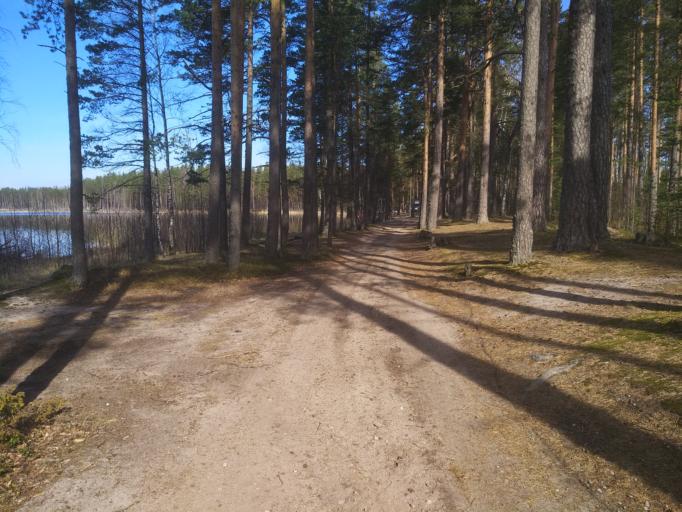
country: RU
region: Leningrad
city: Priozersk
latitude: 60.9194
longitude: 30.3142
